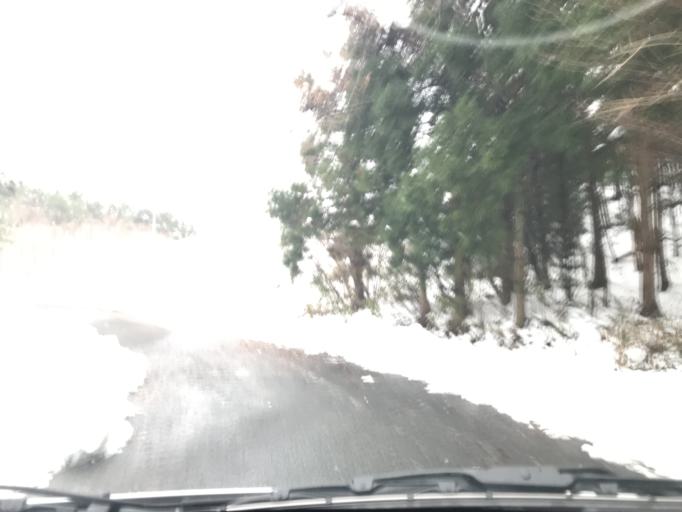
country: JP
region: Iwate
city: Mizusawa
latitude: 39.0424
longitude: 141.0201
